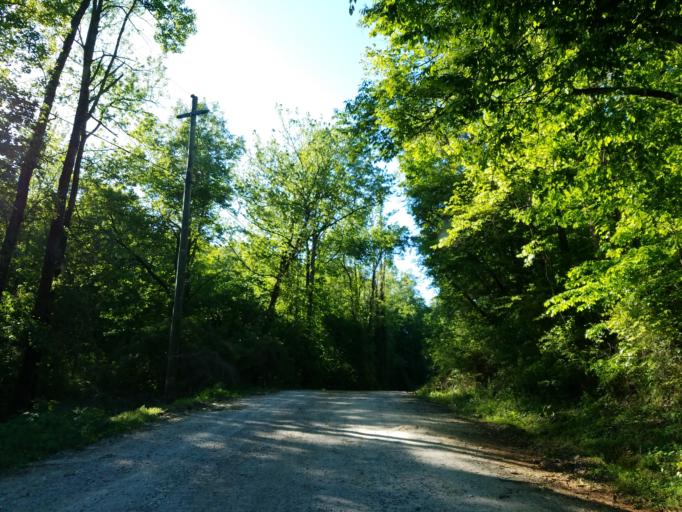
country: US
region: Georgia
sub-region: Gilmer County
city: Ellijay
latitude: 34.6375
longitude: -84.4964
